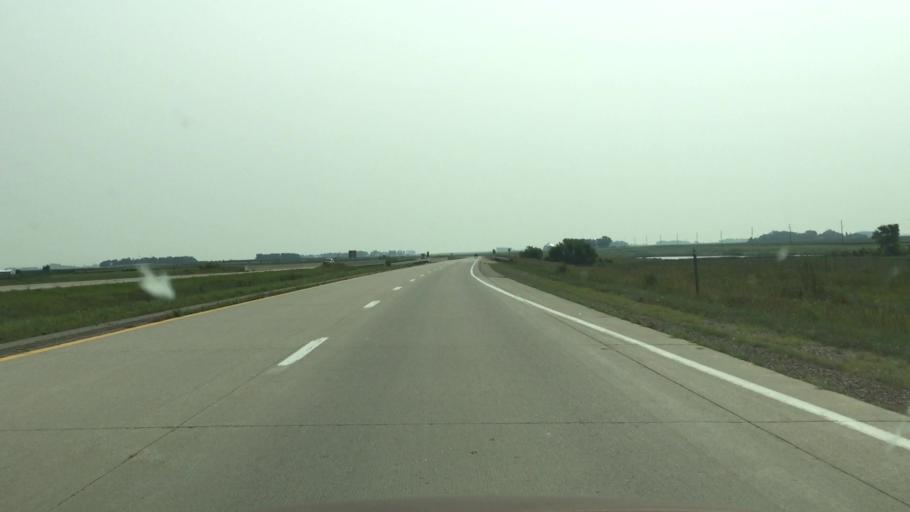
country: US
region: Iowa
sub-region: Osceola County
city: Sibley
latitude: 43.3843
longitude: -95.7400
